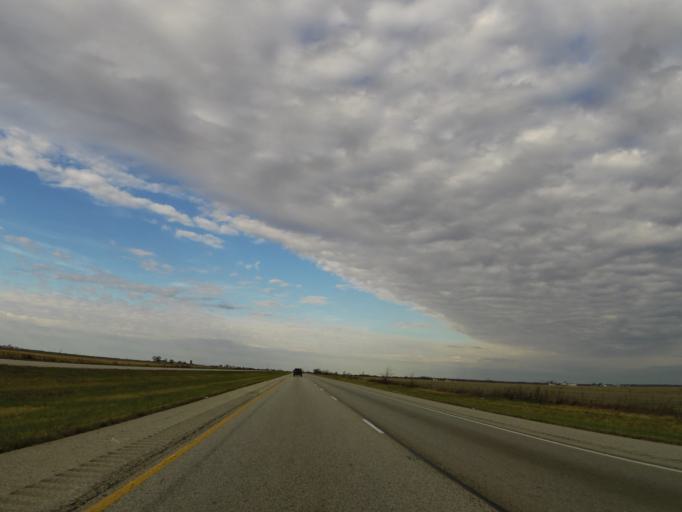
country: US
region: Illinois
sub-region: Washington County
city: Nashville
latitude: 38.4195
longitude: -89.4479
